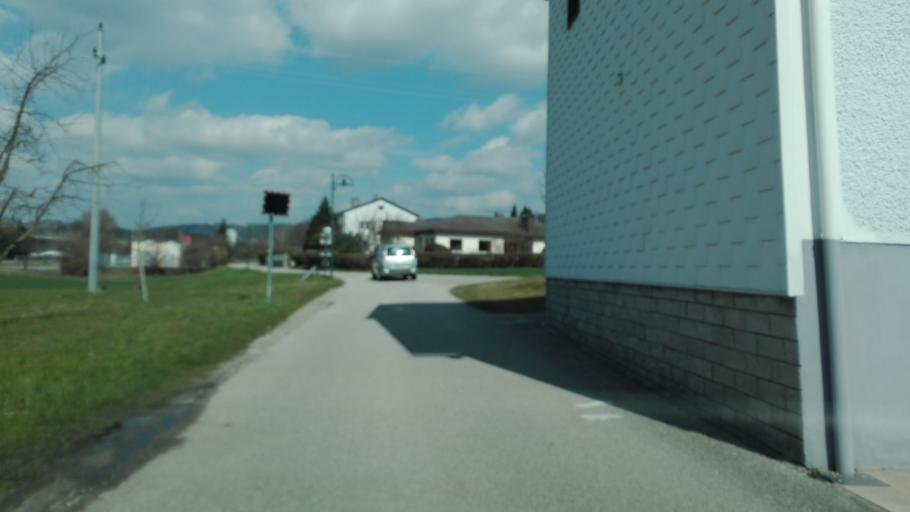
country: AT
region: Upper Austria
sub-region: Politischer Bezirk Urfahr-Umgebung
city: Feldkirchen an der Donau
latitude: 48.3581
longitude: 14.0290
